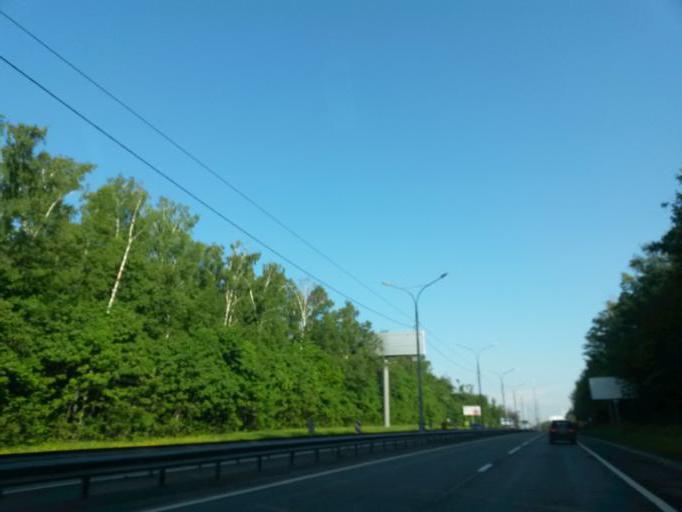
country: RU
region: Moskovskaya
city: Petrovskaya
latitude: 55.5441
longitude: 37.7992
